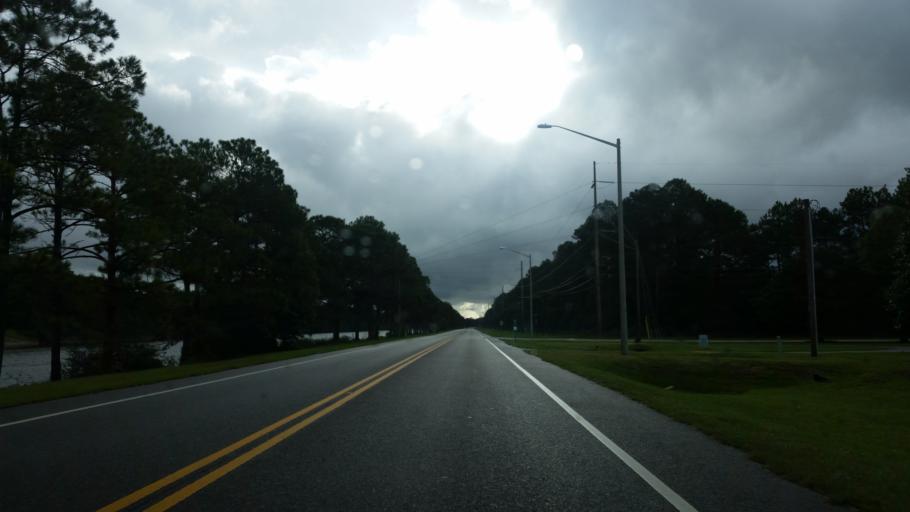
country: US
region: Alabama
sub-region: Baldwin County
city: Gulf Shores
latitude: 30.2793
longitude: -87.6677
